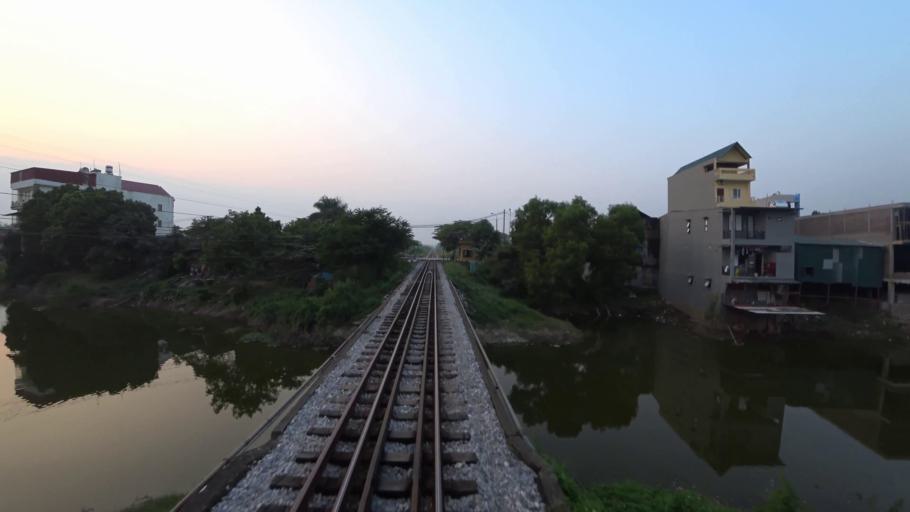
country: VN
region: Ha Noi
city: Dong Anh
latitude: 21.1266
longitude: 105.8799
